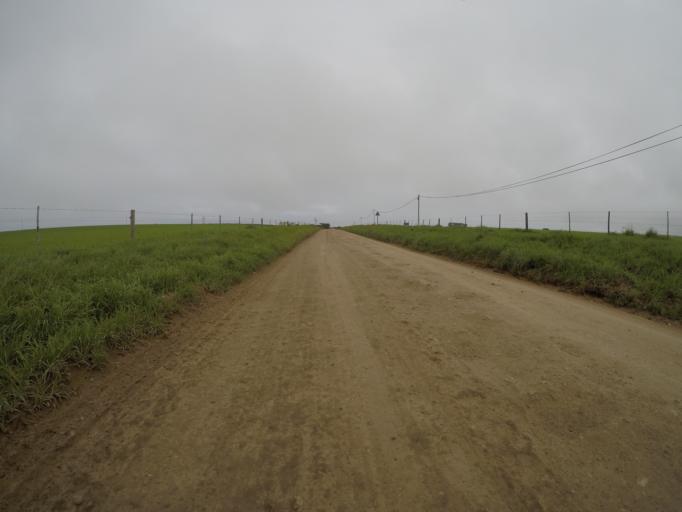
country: ZA
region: Eastern Cape
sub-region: Cacadu District Municipality
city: Kareedouw
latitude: -34.0689
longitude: 24.2382
